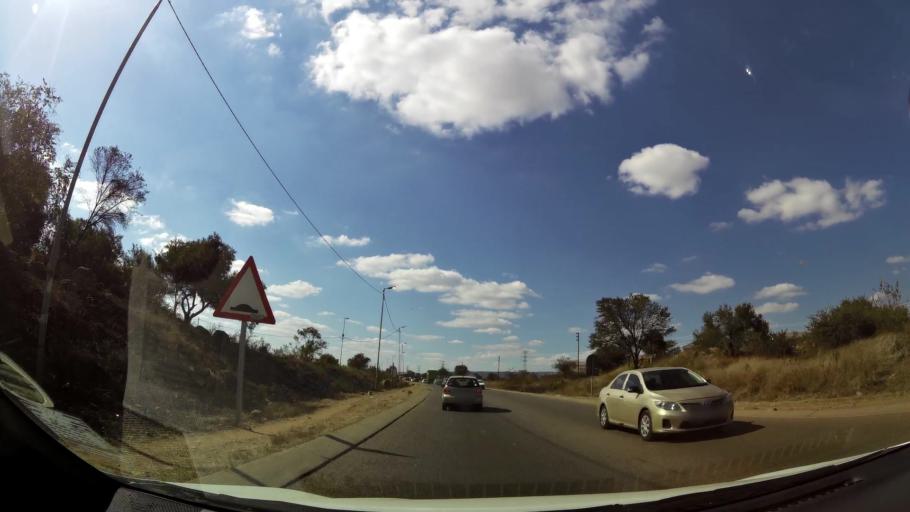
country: ZA
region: Gauteng
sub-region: City of Tshwane Metropolitan Municipality
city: Cullinan
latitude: -25.7387
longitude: 28.3908
